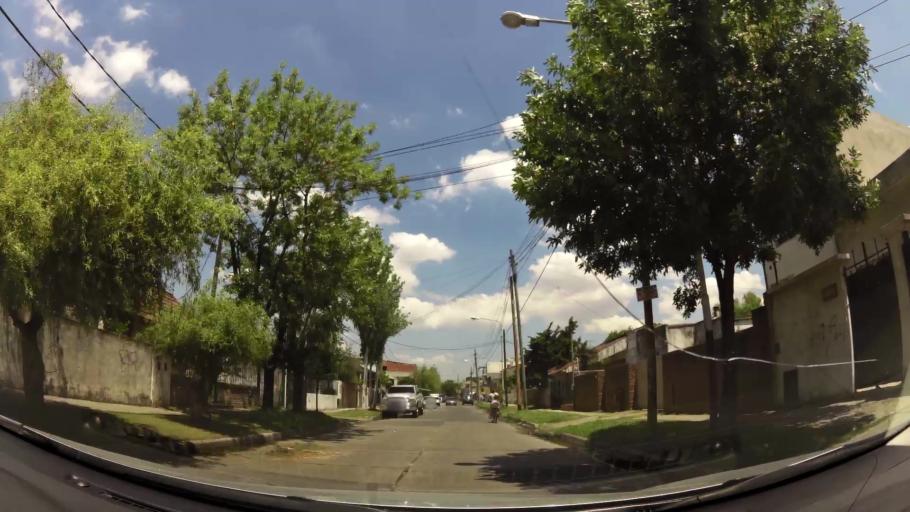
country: AR
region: Buenos Aires
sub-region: Partido de Tigre
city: Tigre
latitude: -34.4160
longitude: -58.5976
